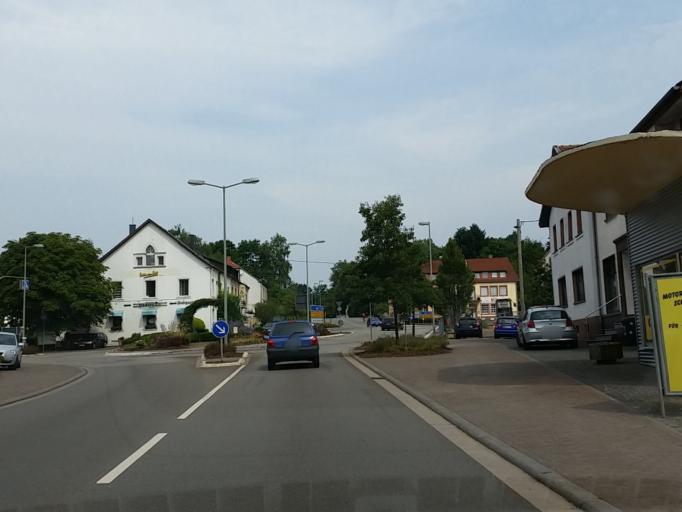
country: DE
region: Saarland
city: Schmelz
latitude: 49.4899
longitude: 6.8375
